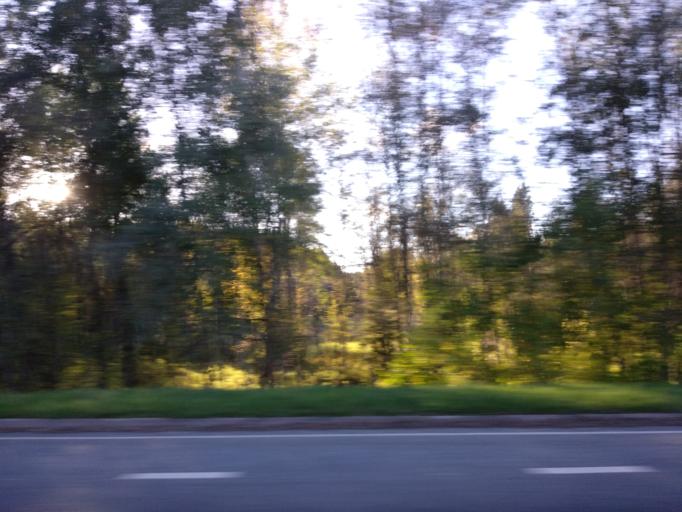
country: EE
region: Polvamaa
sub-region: Polva linn
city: Polva
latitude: 58.0437
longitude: 27.0657
